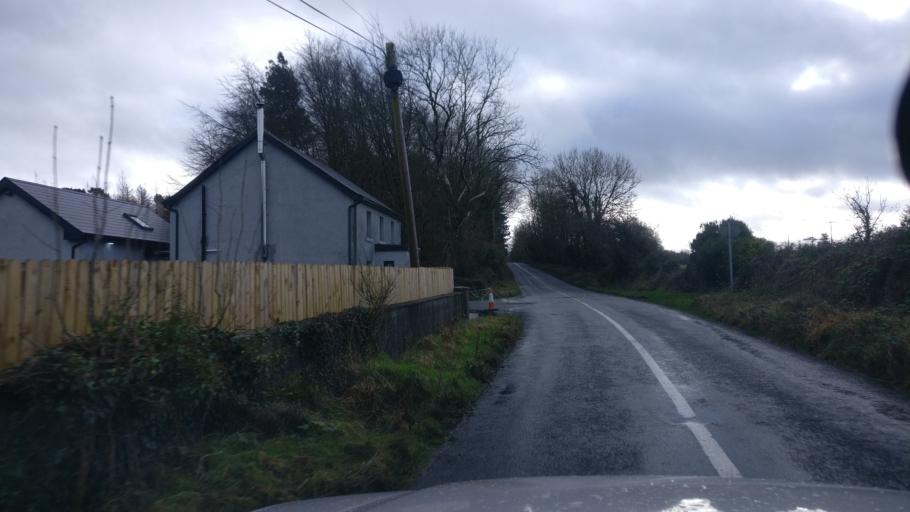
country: IE
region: Connaught
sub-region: County Galway
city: Loughrea
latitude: 53.2500
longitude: -8.6227
